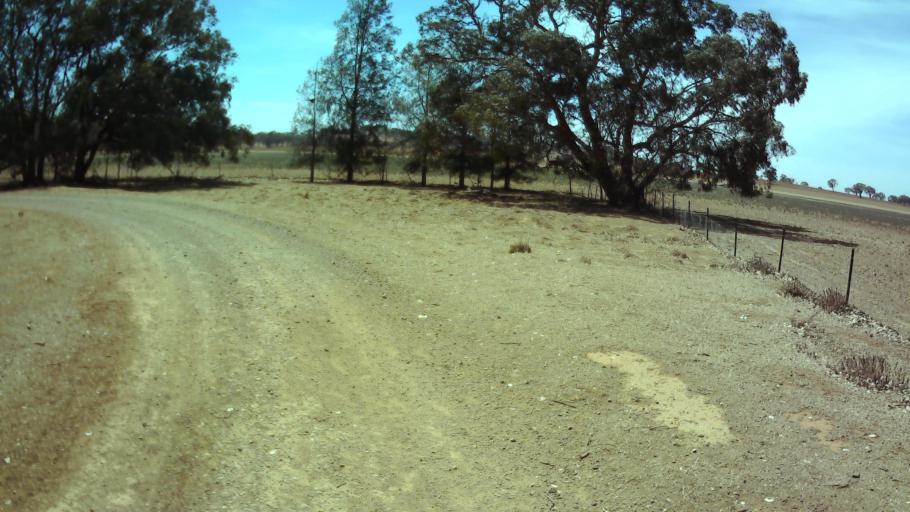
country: AU
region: New South Wales
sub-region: Weddin
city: Grenfell
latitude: -33.9822
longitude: 148.1651
